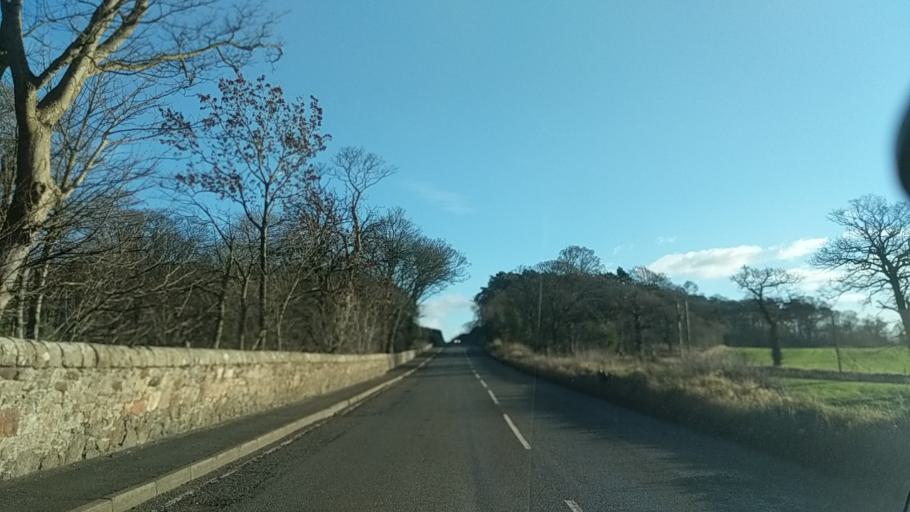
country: GB
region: Scotland
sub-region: Edinburgh
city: Queensferry
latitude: 55.9881
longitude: -3.3698
